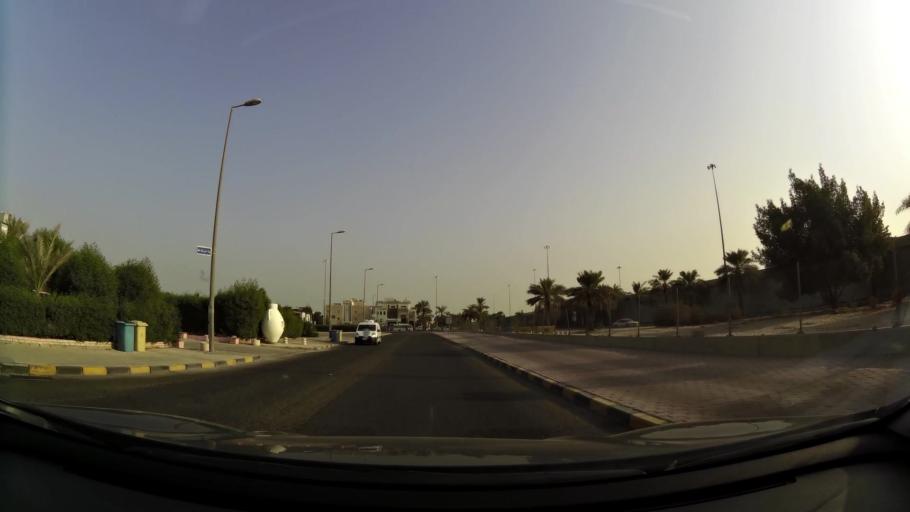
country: KW
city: Bayan
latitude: 29.3059
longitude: 48.0605
